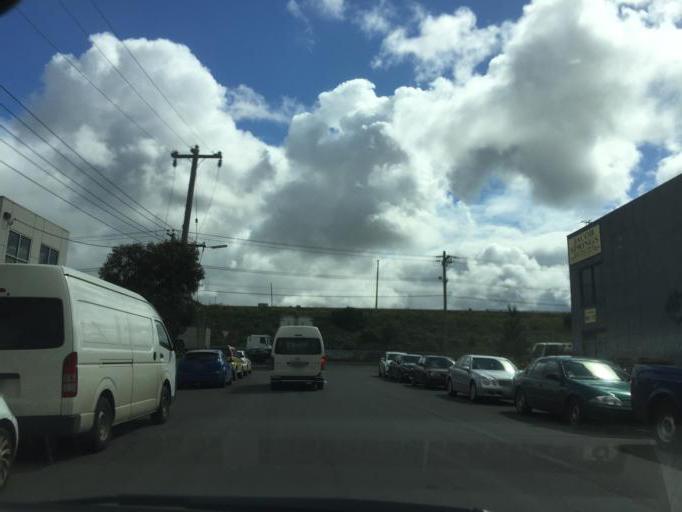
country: AU
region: Victoria
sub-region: Maribyrnong
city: Braybrook
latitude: -37.7987
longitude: 144.8496
